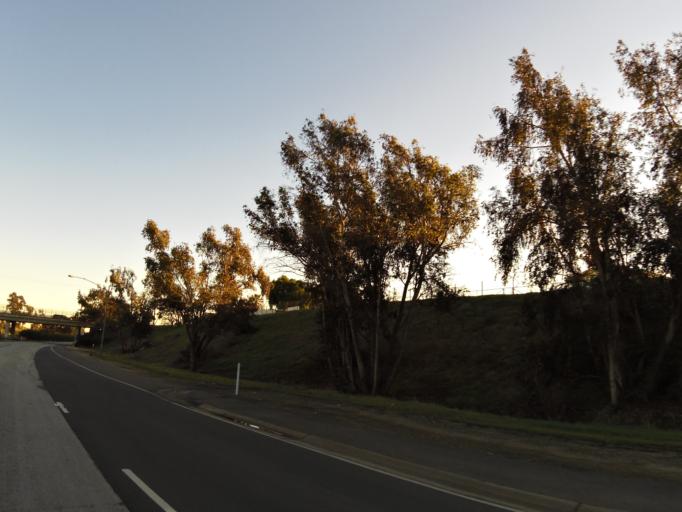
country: US
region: California
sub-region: Monterey County
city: Greenfield
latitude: 36.3220
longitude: -121.2368
